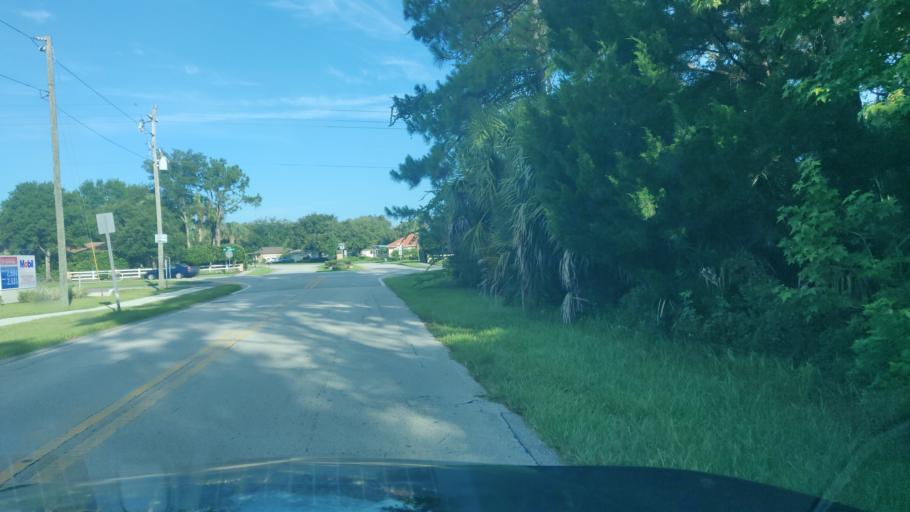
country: US
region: Florida
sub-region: Flagler County
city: Palm Coast
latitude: 29.5298
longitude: -81.2377
